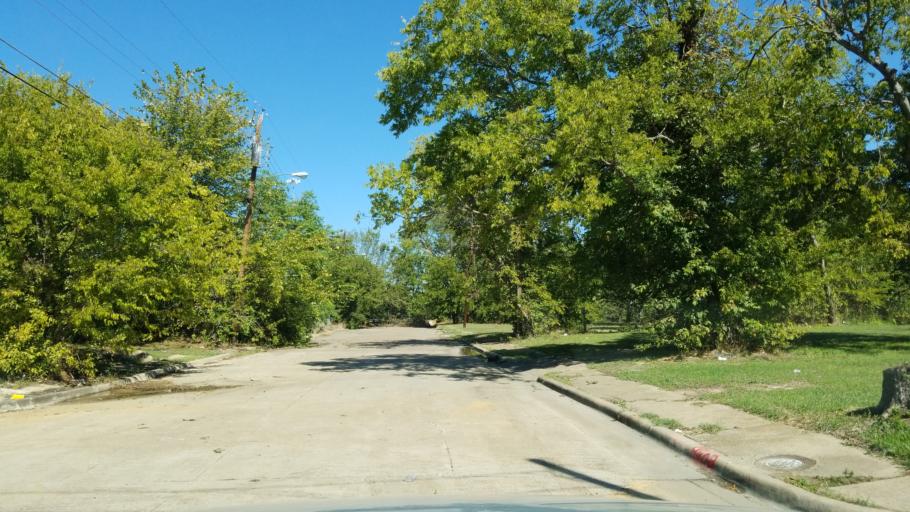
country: US
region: Texas
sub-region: Dallas County
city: Dallas
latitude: 32.7786
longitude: -96.7457
